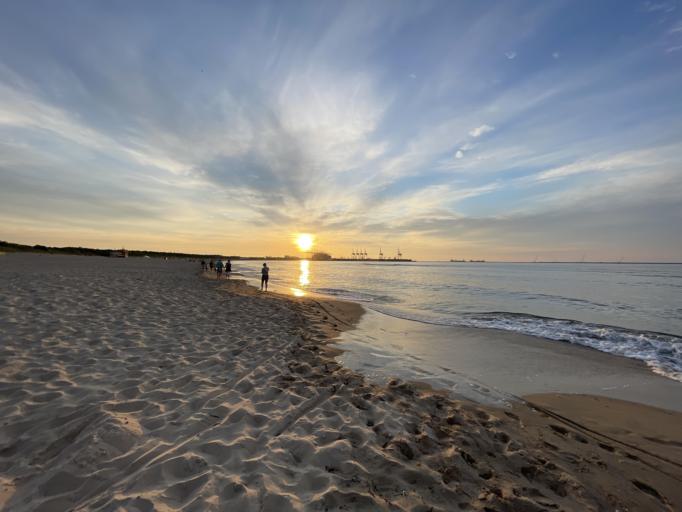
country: PL
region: Pomeranian Voivodeship
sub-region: Gdansk
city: Gdansk
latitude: 54.3742
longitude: 18.7380
